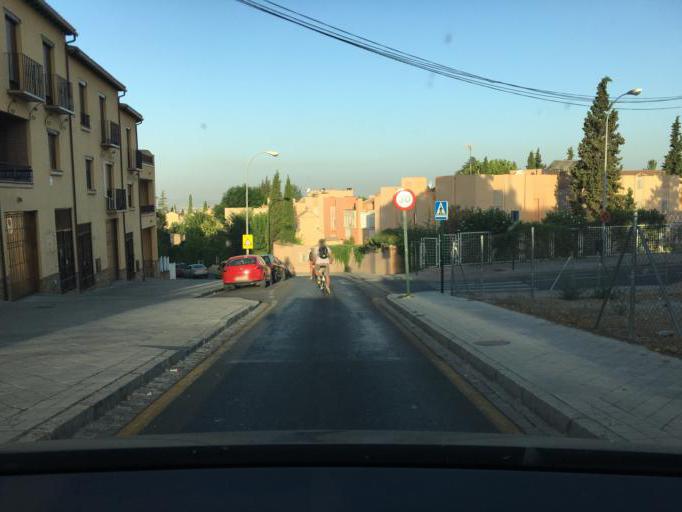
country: ES
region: Andalusia
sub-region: Provincia de Granada
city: Granada
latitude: 37.1869
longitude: -3.5934
